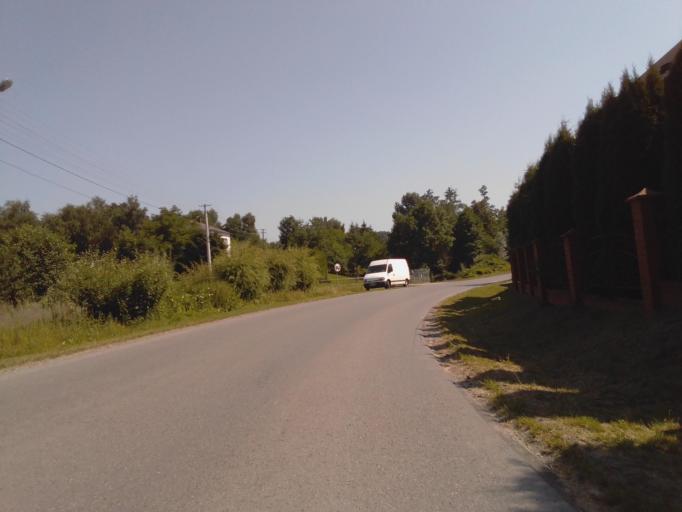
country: PL
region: Subcarpathian Voivodeship
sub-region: Powiat ropczycko-sedziszowski
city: Zagorzyce
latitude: 50.0353
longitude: 21.6531
